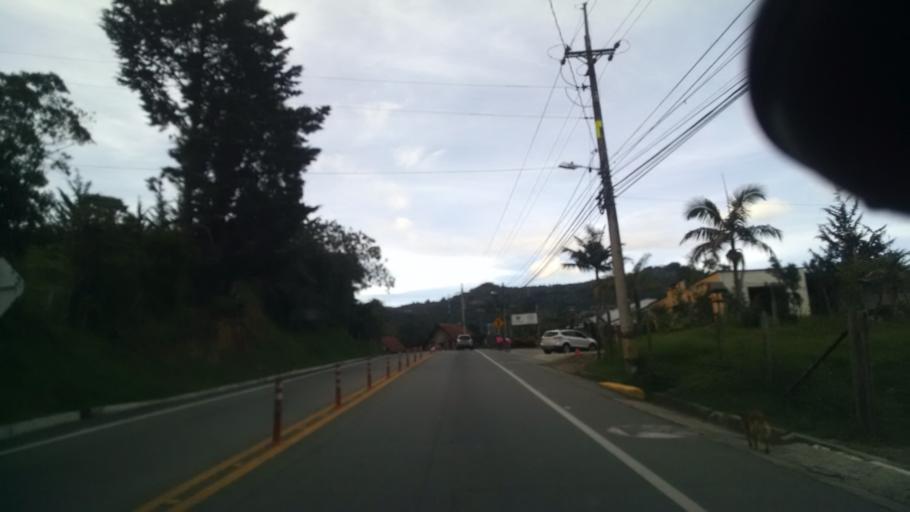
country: CO
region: Antioquia
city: El Retiro
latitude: 6.1184
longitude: -75.5007
